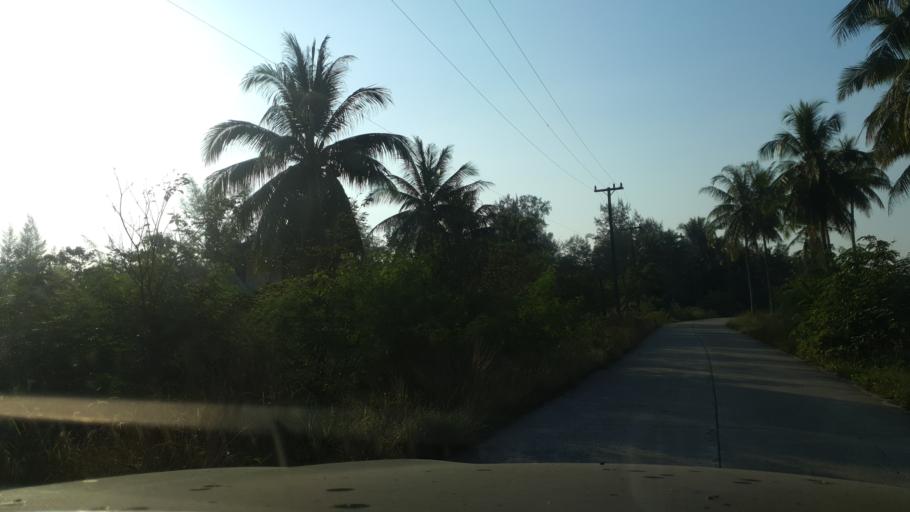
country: TH
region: Prachuap Khiri Khan
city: Bang Saphan
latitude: 11.2816
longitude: 99.5491
